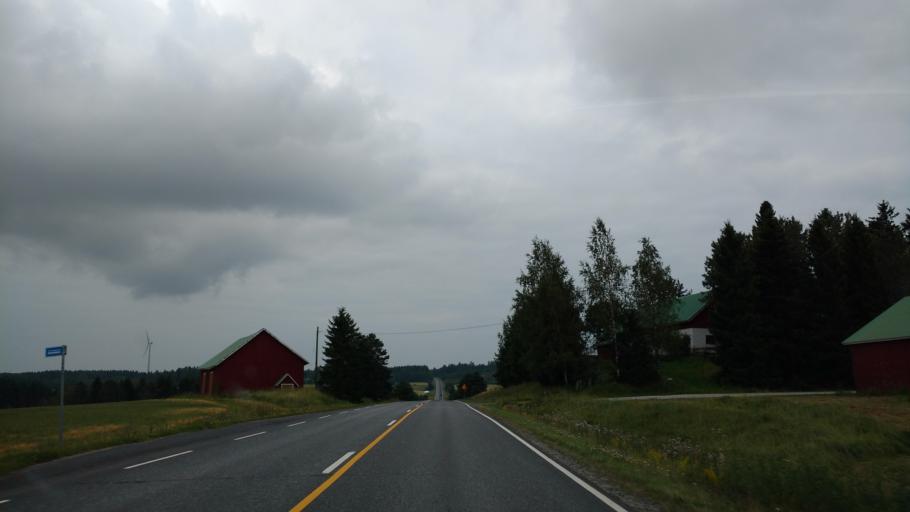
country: FI
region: Varsinais-Suomi
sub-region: Salo
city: Halikko
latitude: 60.4751
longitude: 23.0128
